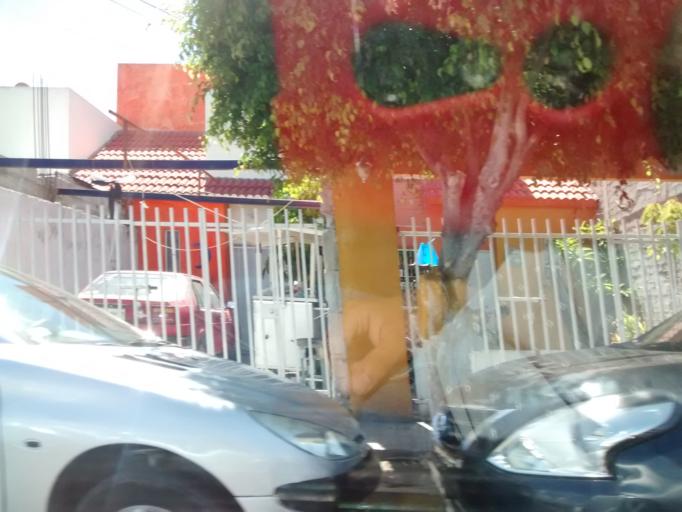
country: MX
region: Puebla
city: Tehuacan
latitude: 18.4696
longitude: -97.4122
